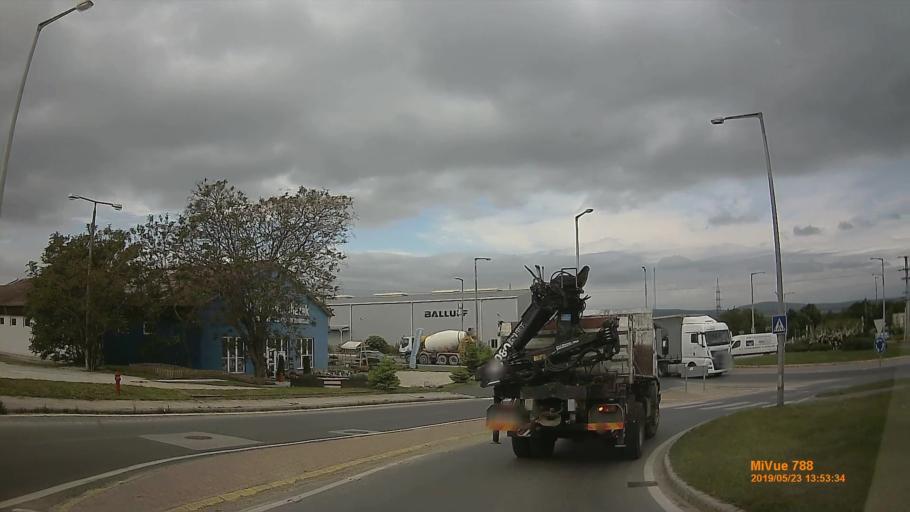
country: HU
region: Veszprem
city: Veszprem
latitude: 47.1156
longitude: 17.9015
